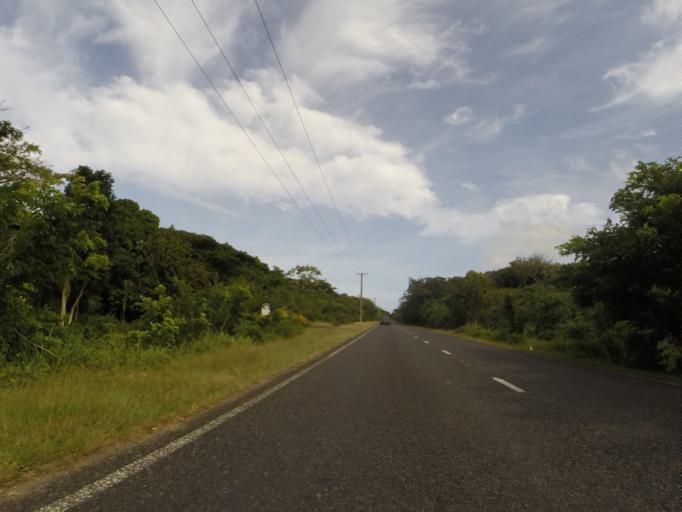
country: FJ
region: Western
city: Nadi
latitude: -18.1498
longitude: 177.4385
